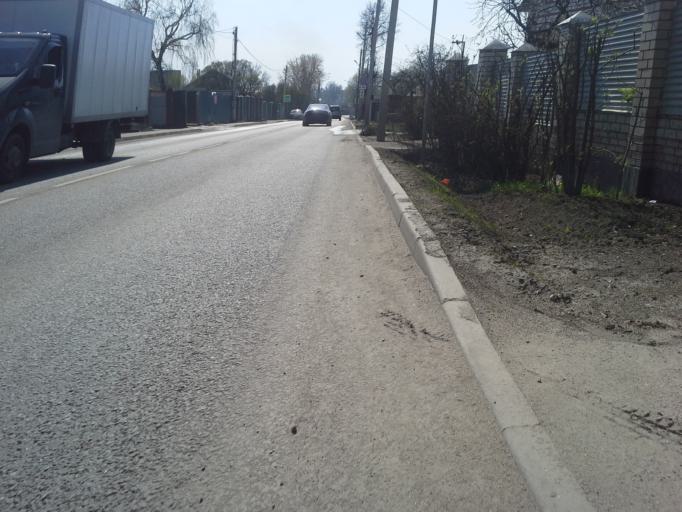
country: RU
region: Moskovskaya
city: Shcherbinka
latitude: 55.4997
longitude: 37.5124
